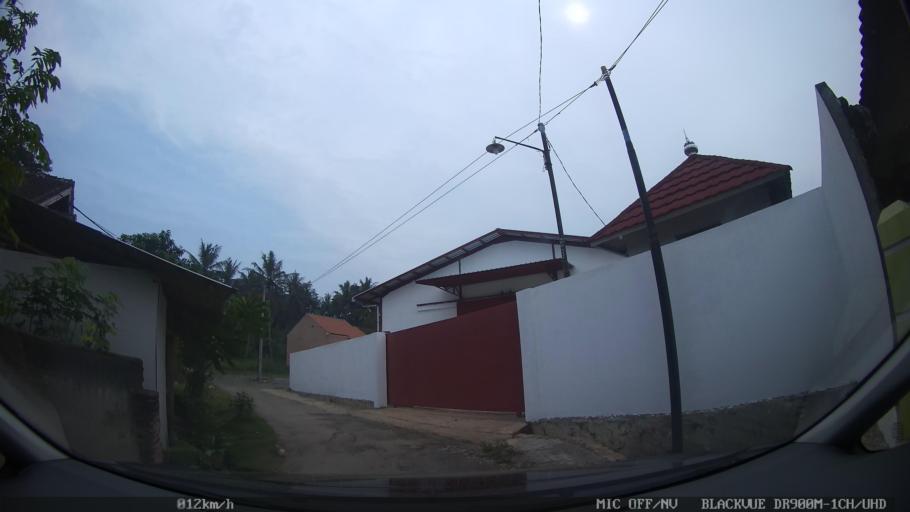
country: ID
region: Lampung
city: Panjang
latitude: -5.4319
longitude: 105.3349
